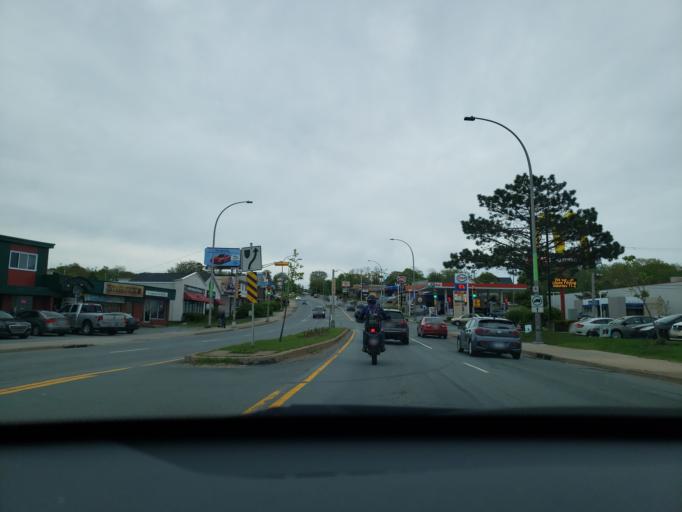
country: CA
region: Nova Scotia
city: Dartmouth
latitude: 44.6820
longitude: -63.5382
